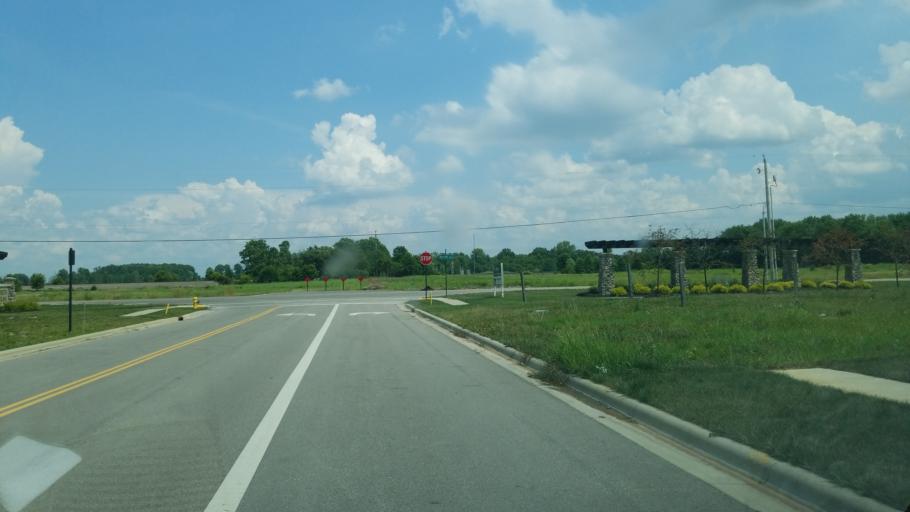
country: US
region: Ohio
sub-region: Delaware County
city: Lewis Center
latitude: 40.2081
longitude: -83.0142
